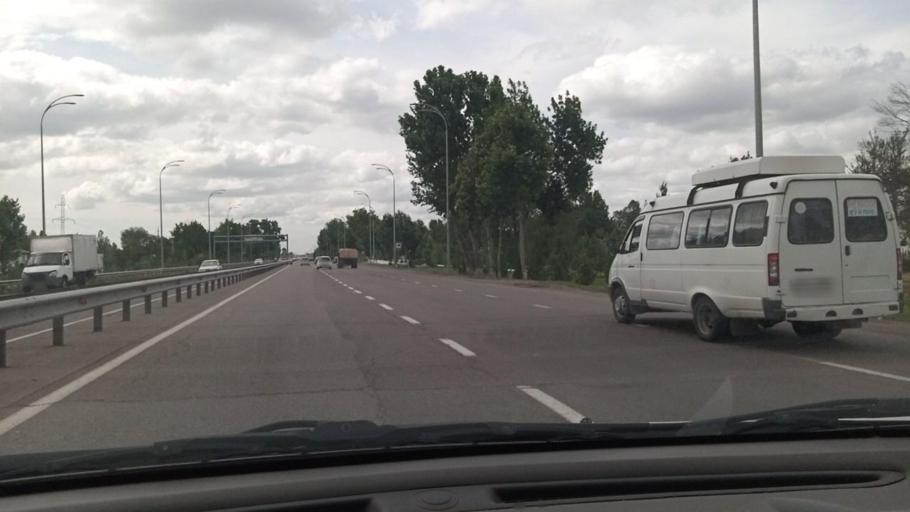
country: UZ
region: Toshkent Shahri
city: Bektemir
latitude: 41.2498
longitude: 69.3899
